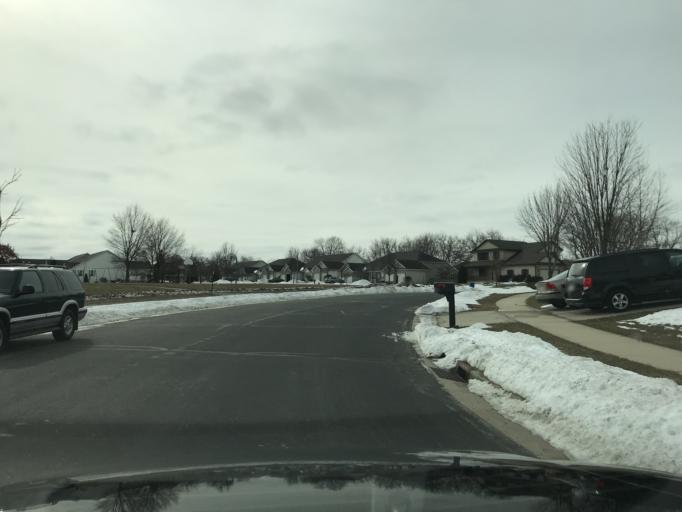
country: US
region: Wisconsin
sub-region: Dane County
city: Monona
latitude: 43.0892
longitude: -89.2704
